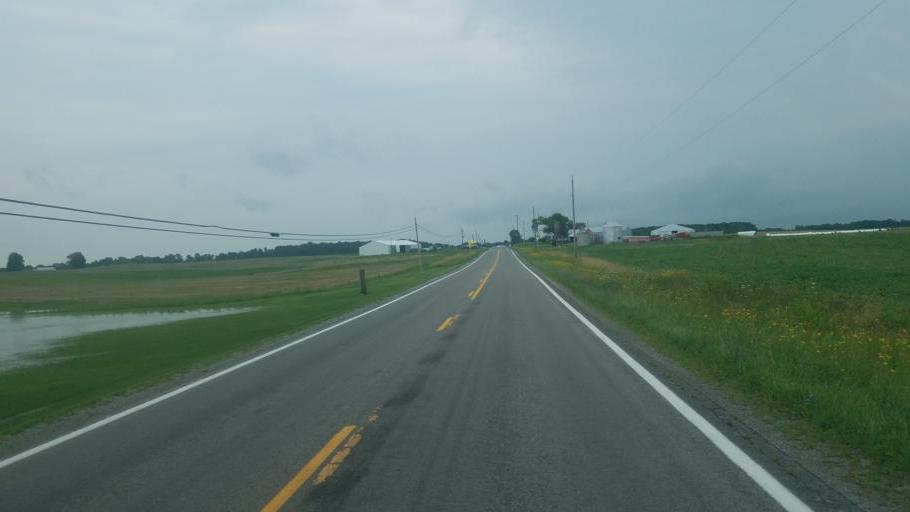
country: US
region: Ohio
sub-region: Hardin County
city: Kenton
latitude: 40.6177
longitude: -83.6653
